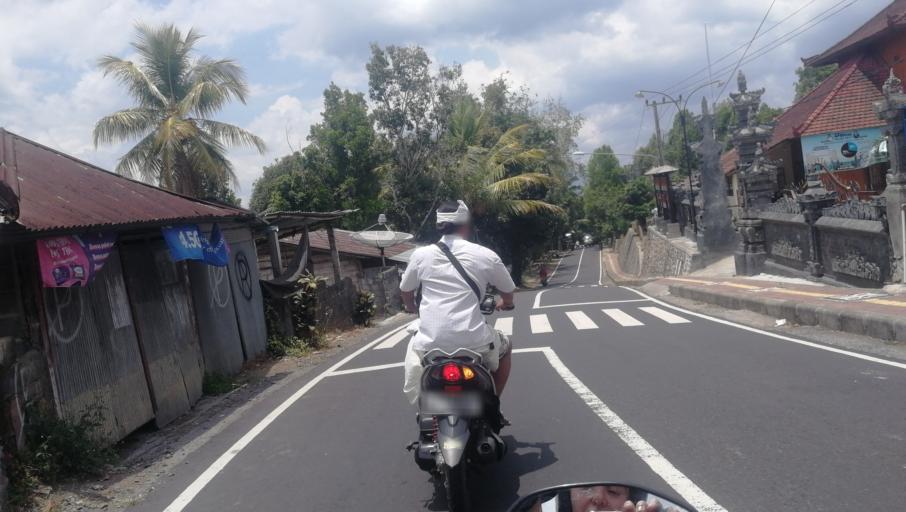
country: ID
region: Bali
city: Munduk
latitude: -8.2643
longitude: 115.0491
